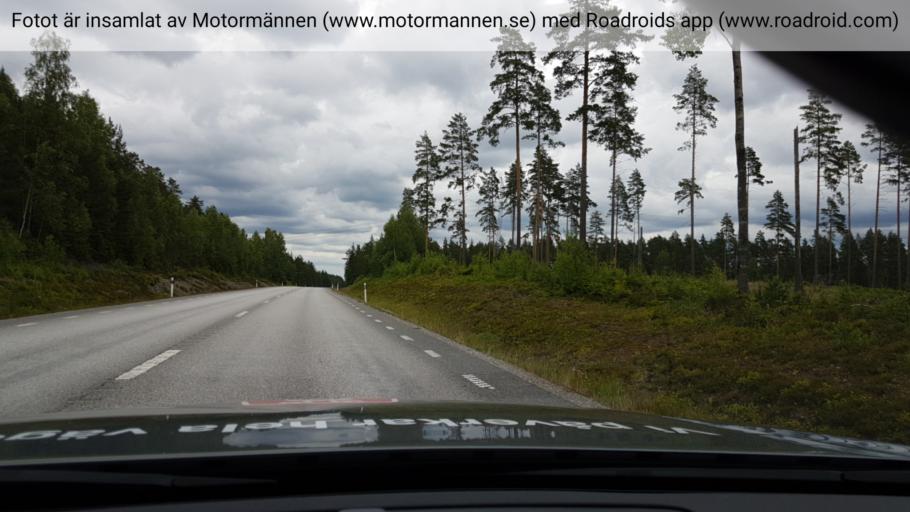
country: SE
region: OErebro
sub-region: Lindesbergs Kommun
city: Lindesberg
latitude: 59.6719
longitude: 15.2908
